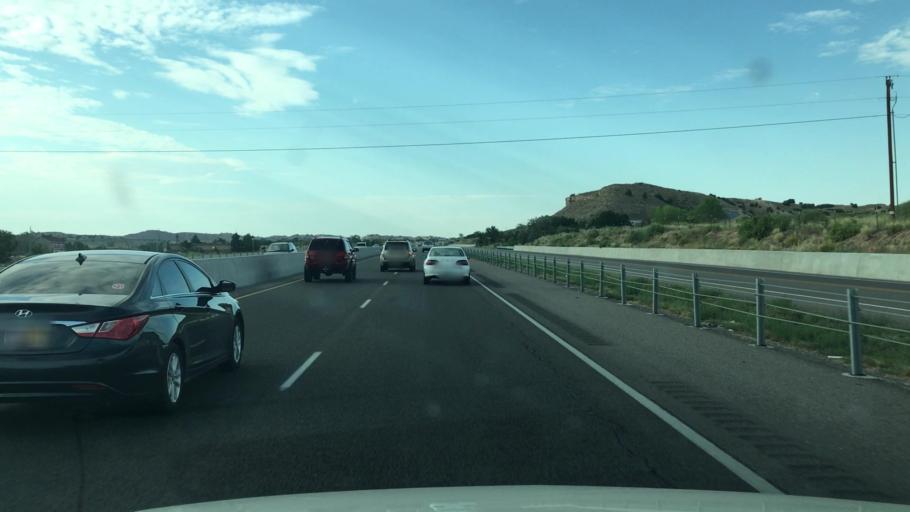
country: US
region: New Mexico
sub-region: Santa Fe County
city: El Valle de Arroyo Seco
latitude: 35.9505
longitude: -106.0210
